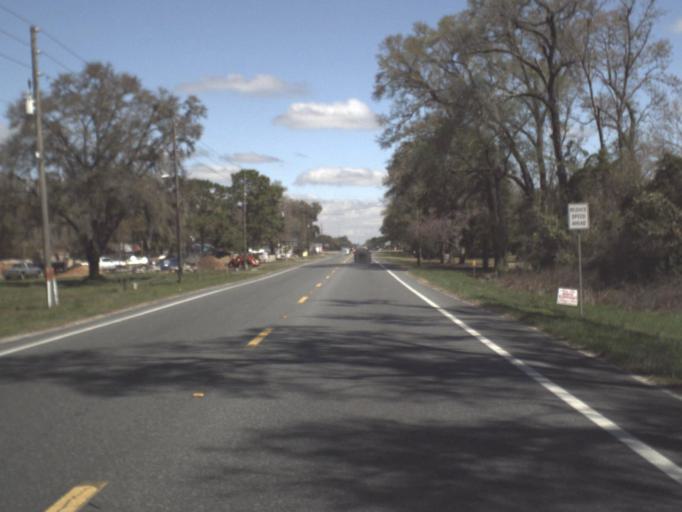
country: US
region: Florida
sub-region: Wakulla County
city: Crawfordville
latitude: 30.1006
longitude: -84.3831
